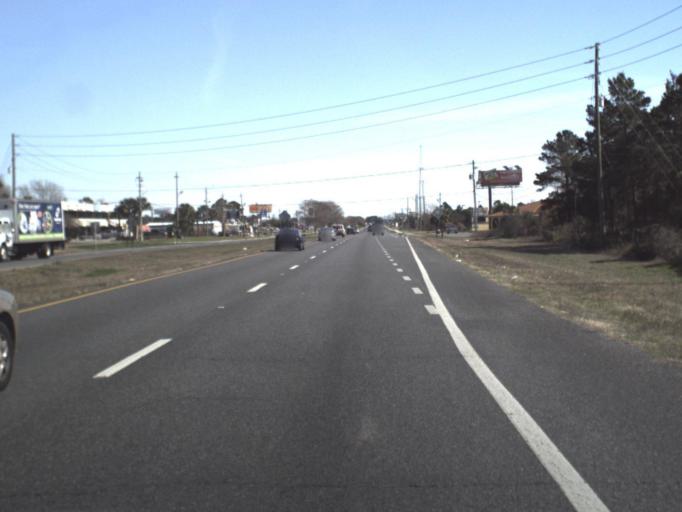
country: US
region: Florida
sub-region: Bay County
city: Laguna Beach
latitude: 30.2331
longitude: -85.8965
